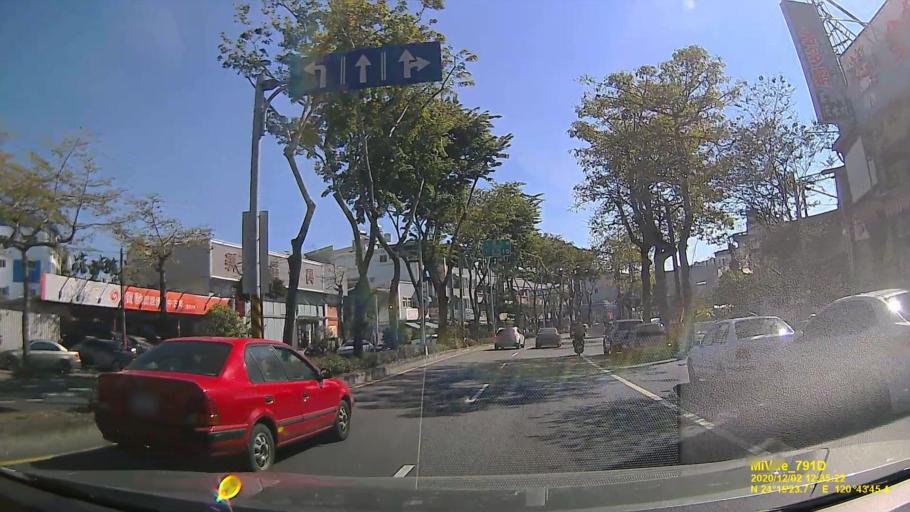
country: TW
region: Taiwan
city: Fengyuan
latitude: 24.2565
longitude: 120.7293
